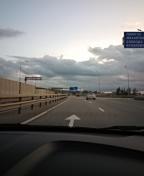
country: RU
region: Moskovskaya
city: Vereya
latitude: 55.5717
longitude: 38.0514
